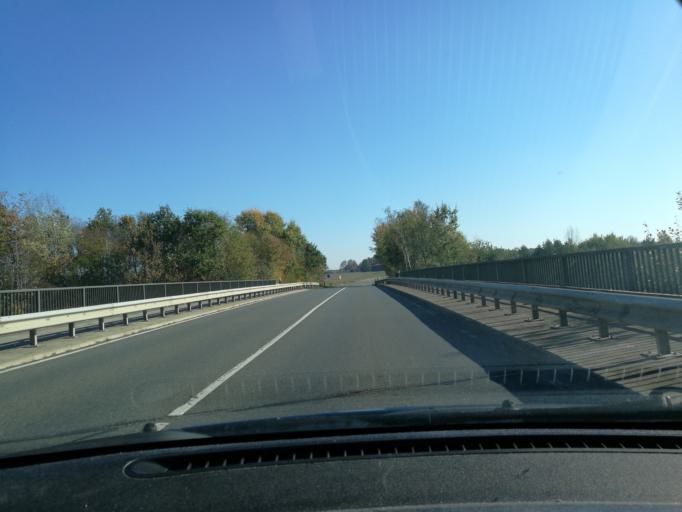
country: DE
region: Lower Saxony
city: Wendisch Evern
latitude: 53.2287
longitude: 10.4510
